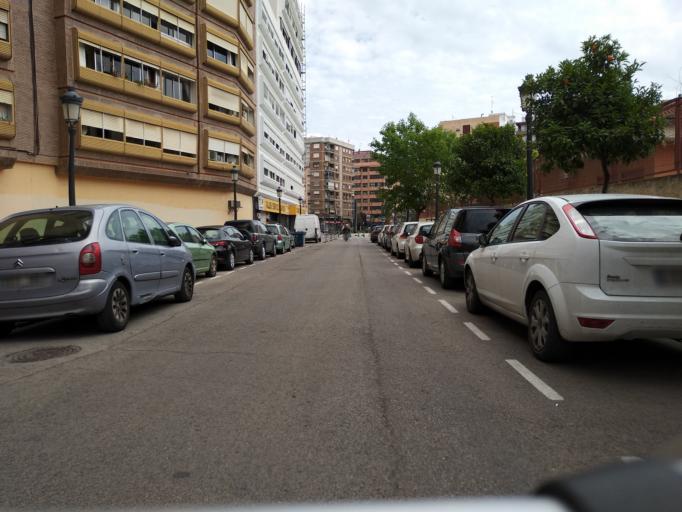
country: ES
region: Valencia
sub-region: Provincia de Valencia
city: Tavernes Blanques
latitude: 39.4883
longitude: -0.3698
